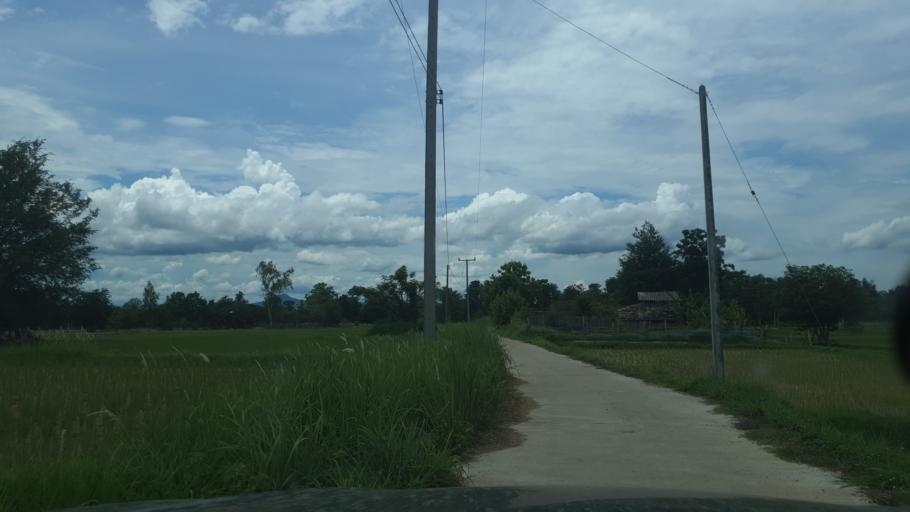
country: TH
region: Lampang
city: Sop Prap
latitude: 17.8632
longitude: 99.3930
